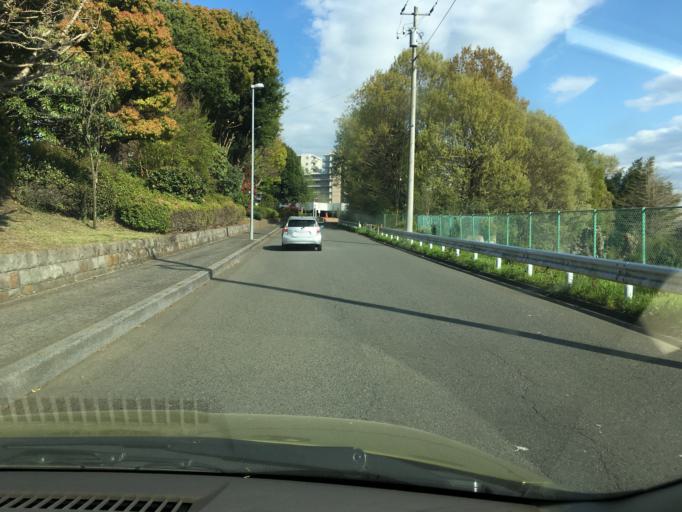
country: JP
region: Tokyo
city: Hachioji
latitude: 35.5820
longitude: 139.3317
